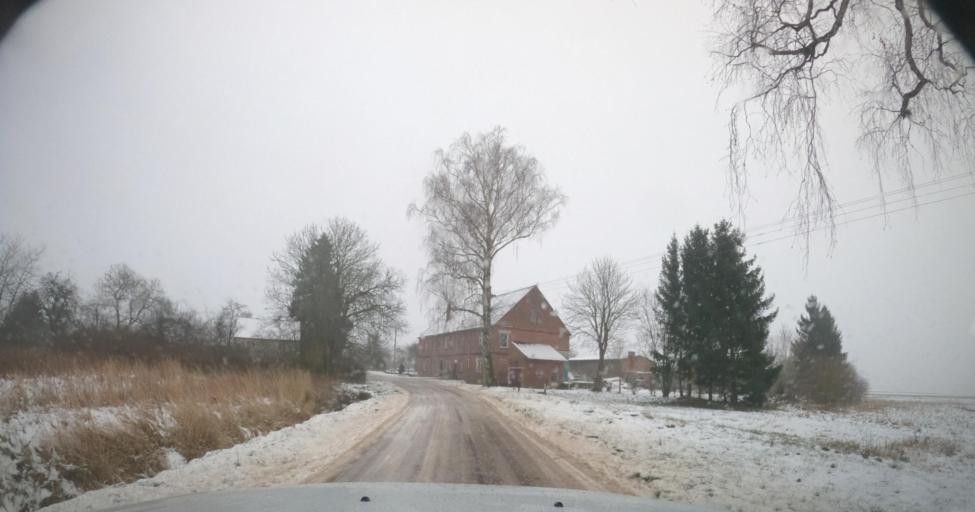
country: PL
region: West Pomeranian Voivodeship
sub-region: Powiat kamienski
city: Golczewo
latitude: 53.8683
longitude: 15.0696
